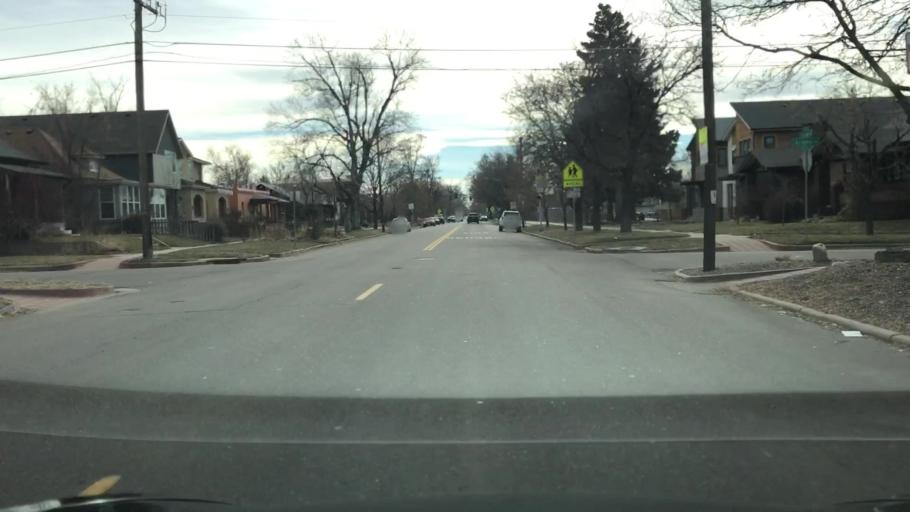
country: US
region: Colorado
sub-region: Denver County
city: Denver
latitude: 39.6950
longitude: -104.9828
